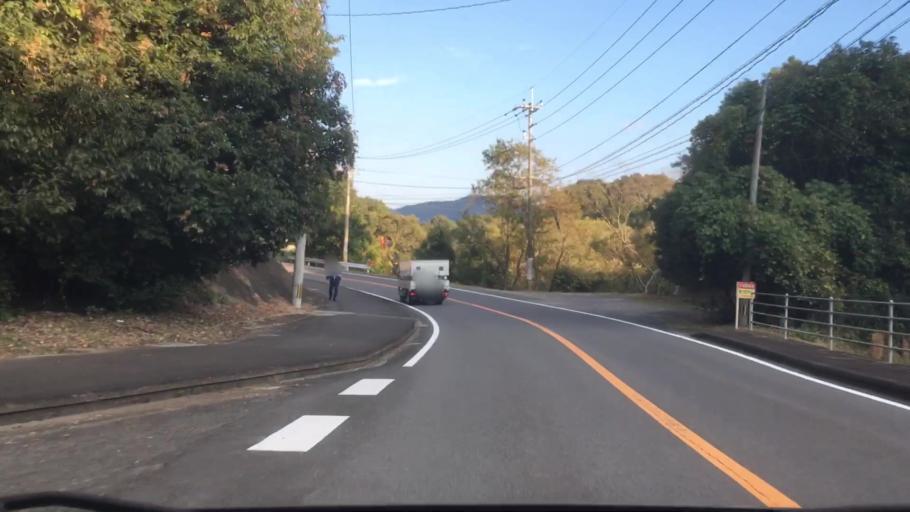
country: JP
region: Nagasaki
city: Sasebo
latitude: 32.9477
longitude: 129.6612
